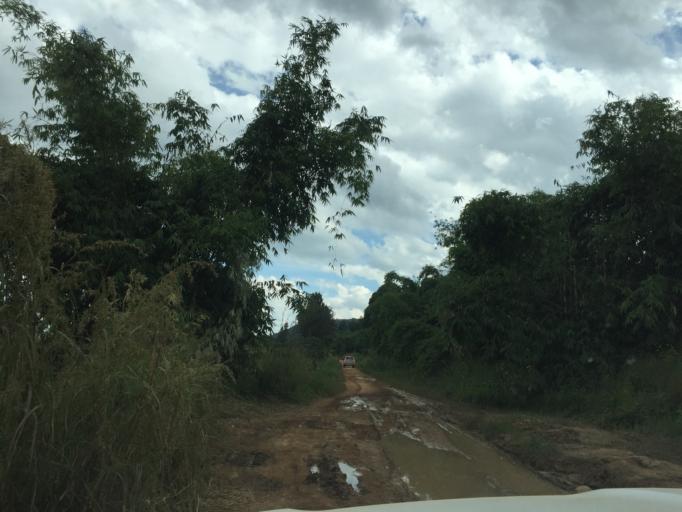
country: TZ
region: Iringa
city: Iringa
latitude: -8.0857
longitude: 35.2719
